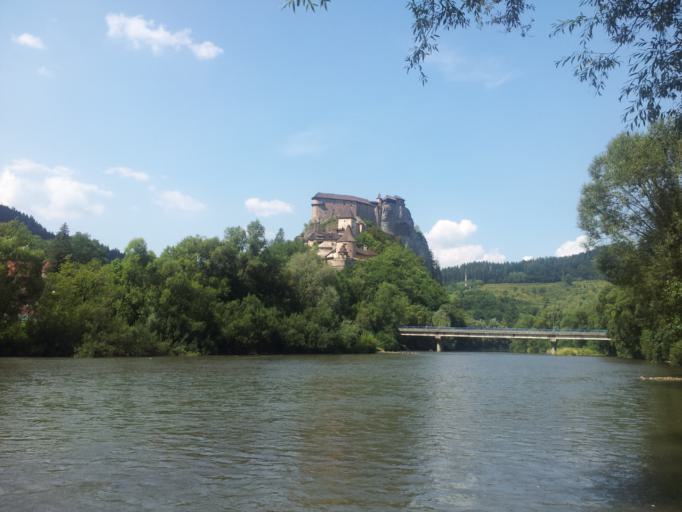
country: SK
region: Zilinsky
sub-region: Okres Dolny Kubin
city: Dolny Kubin
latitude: 49.2587
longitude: 19.3605
